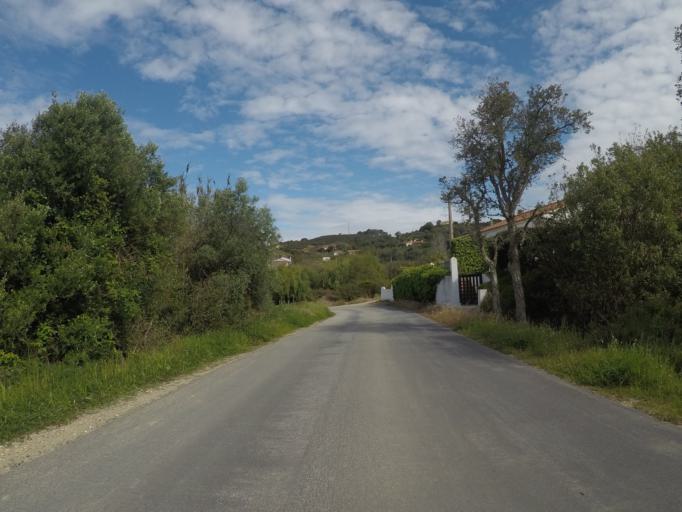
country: PT
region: Beja
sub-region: Odemira
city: Sao Teotonio
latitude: 37.4358
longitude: -8.7831
